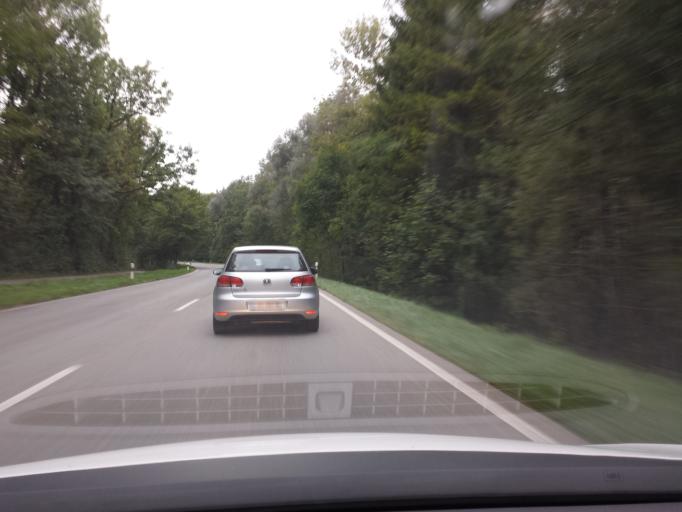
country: DE
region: Bavaria
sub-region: Upper Bavaria
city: Piding
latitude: 47.7584
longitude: 12.9216
